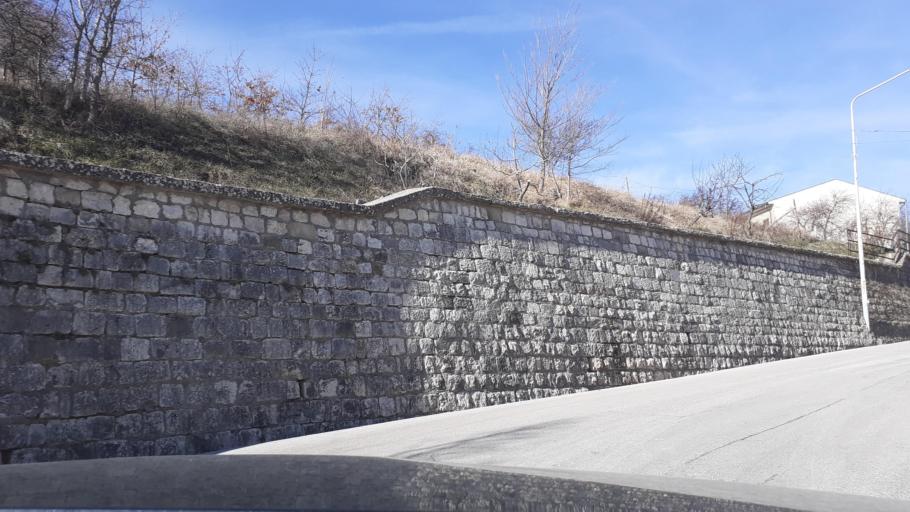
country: IT
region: Molise
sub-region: Provincia di Campobasso
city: Pietracupa
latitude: 41.6816
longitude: 14.5173
